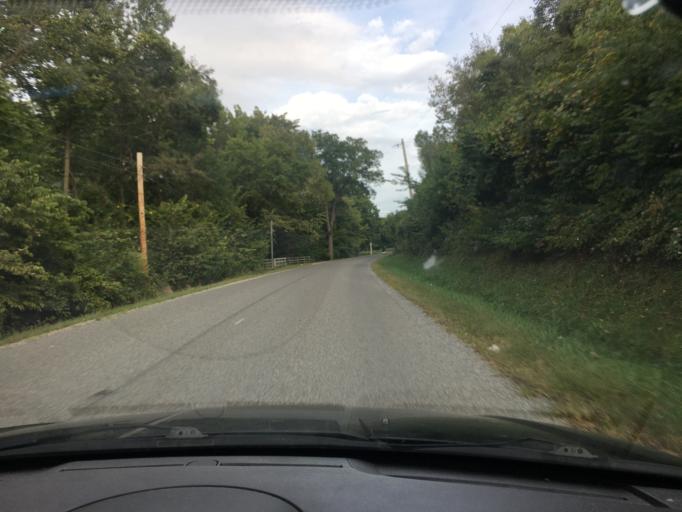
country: US
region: Ohio
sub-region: Logan County
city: West Liberty
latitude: 40.3020
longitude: -83.6970
